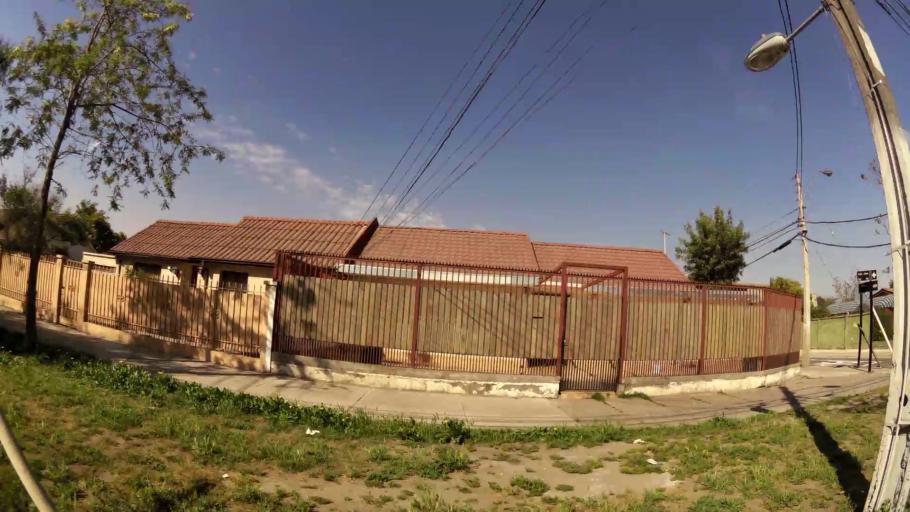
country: CL
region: Santiago Metropolitan
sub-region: Provincia de Santiago
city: La Pintana
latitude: -33.5241
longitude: -70.6099
